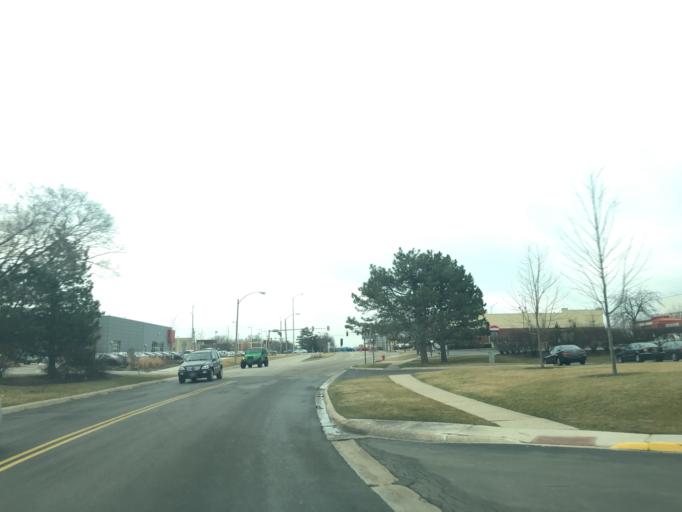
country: US
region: Illinois
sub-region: Cook County
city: Hoffman Estates
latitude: 42.0508
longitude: -88.0866
